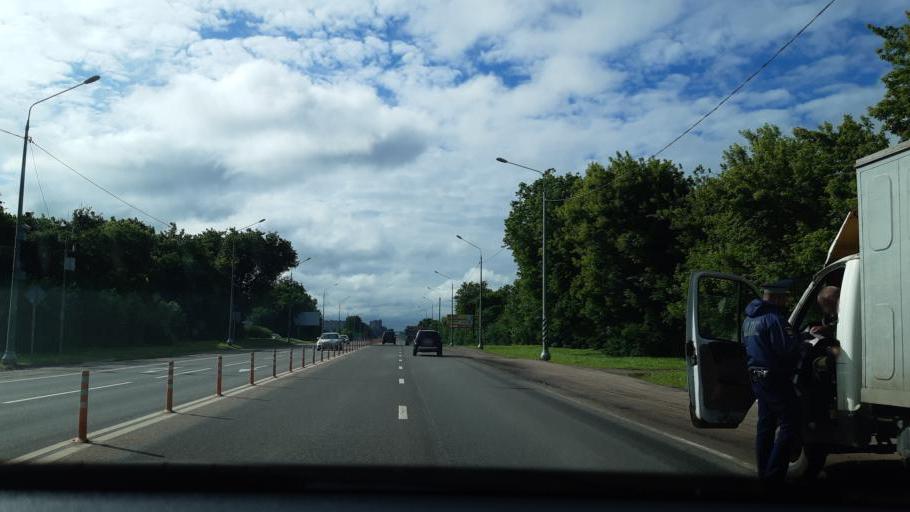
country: RU
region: Smolensk
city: Smolensk
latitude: 54.7522
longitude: 32.0754
